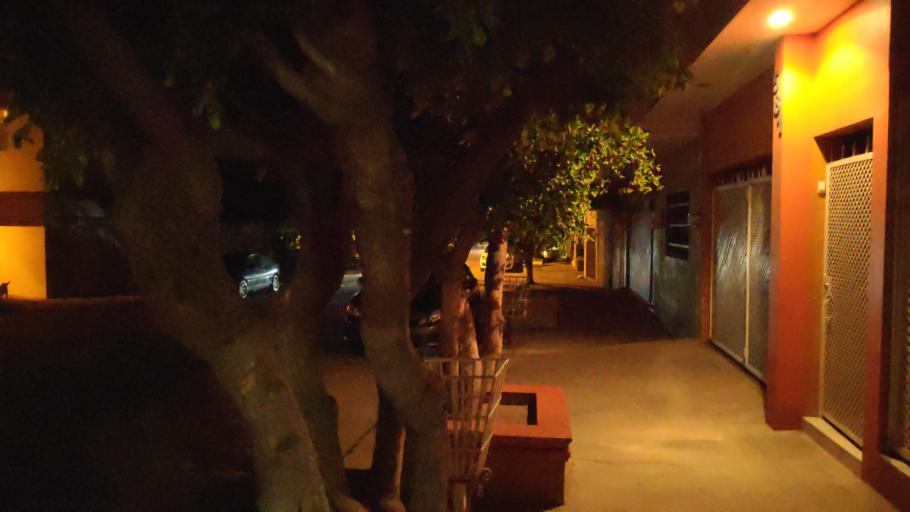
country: MX
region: Sinaloa
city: Culiacan
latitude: 24.7978
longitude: -107.3860
